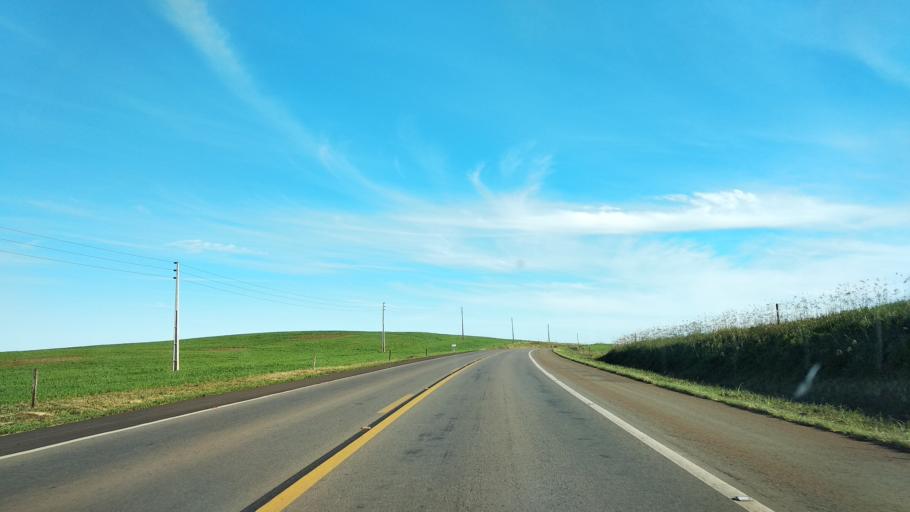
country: BR
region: Santa Catarina
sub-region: Celso Ramos
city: Celso Ramos
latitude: -27.5211
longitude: -51.3522
